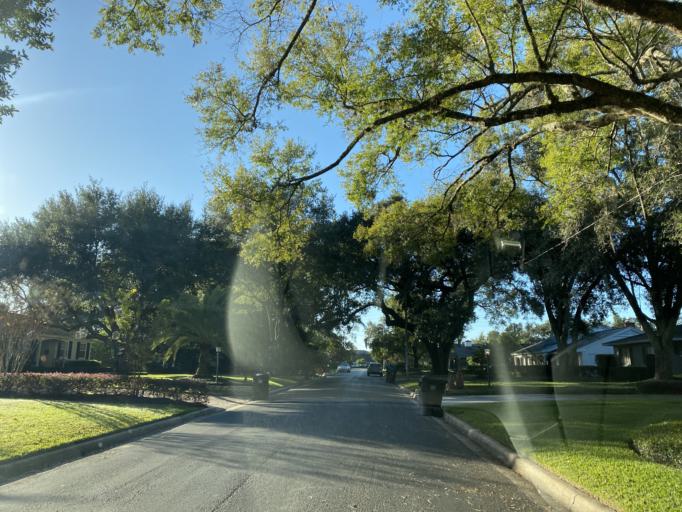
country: US
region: Florida
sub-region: Orange County
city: Orlando
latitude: 28.5559
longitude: -81.4045
